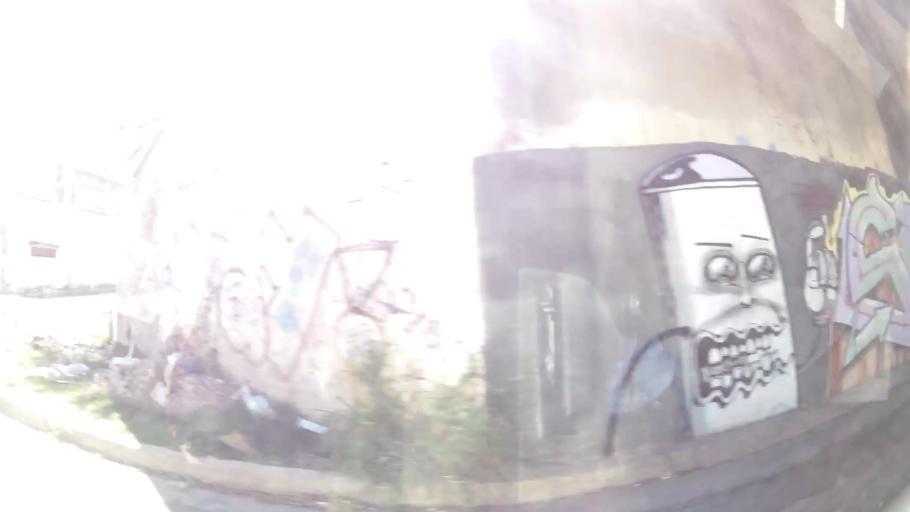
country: AR
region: Cordoba
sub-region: Departamento de Capital
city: Cordoba
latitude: -31.4267
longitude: -64.1586
